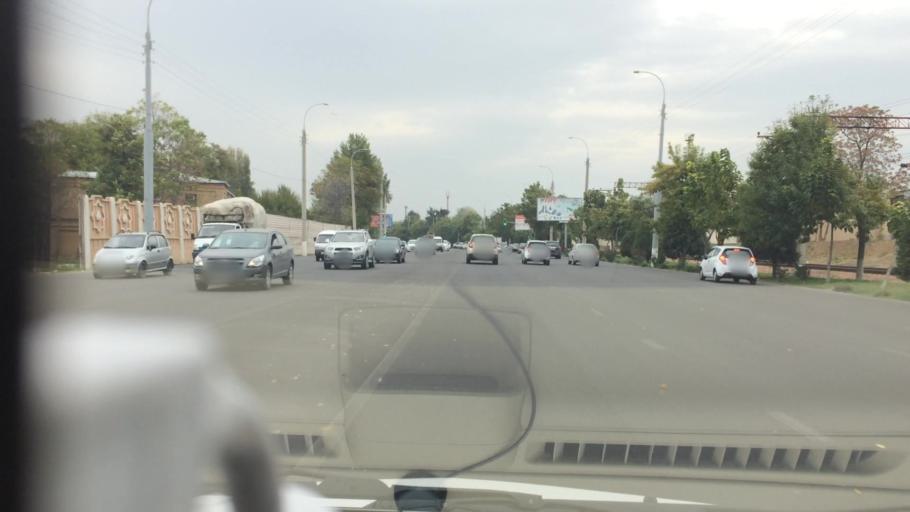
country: UZ
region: Toshkent Shahri
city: Tashkent
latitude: 41.3085
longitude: 69.3034
